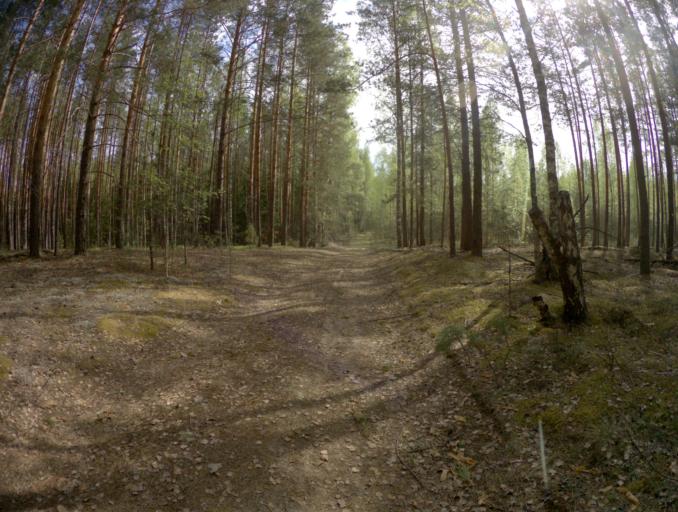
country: RU
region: Ivanovo
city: Yuzha
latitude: 56.5160
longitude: 42.1072
